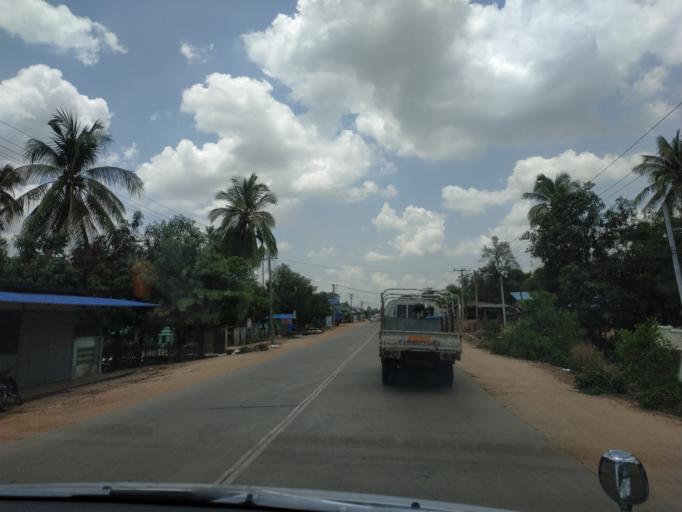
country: MM
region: Bago
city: Bago
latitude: 17.4756
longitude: 96.5230
